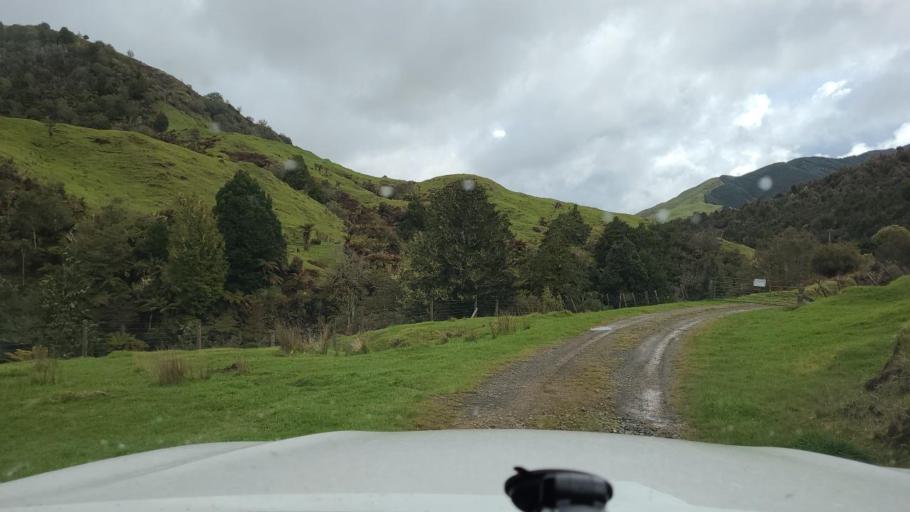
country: NZ
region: Bay of Plenty
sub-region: Opotiki District
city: Opotiki
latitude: -38.2157
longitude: 177.6097
